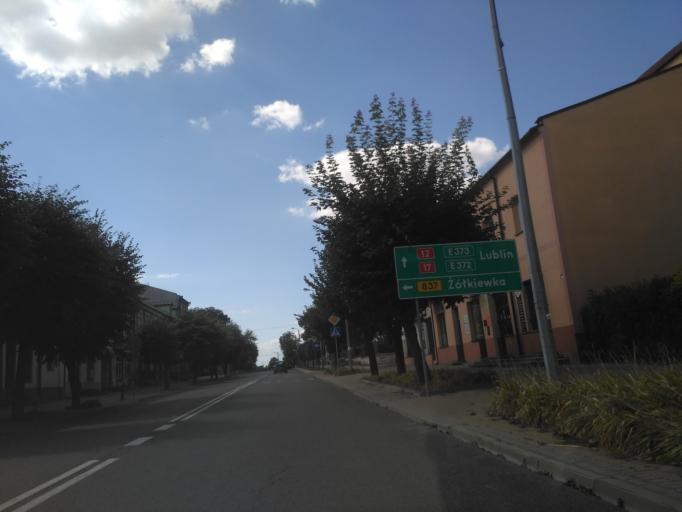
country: PL
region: Lublin Voivodeship
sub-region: Powiat swidnicki
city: Piaski
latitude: 51.1385
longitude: 22.8500
